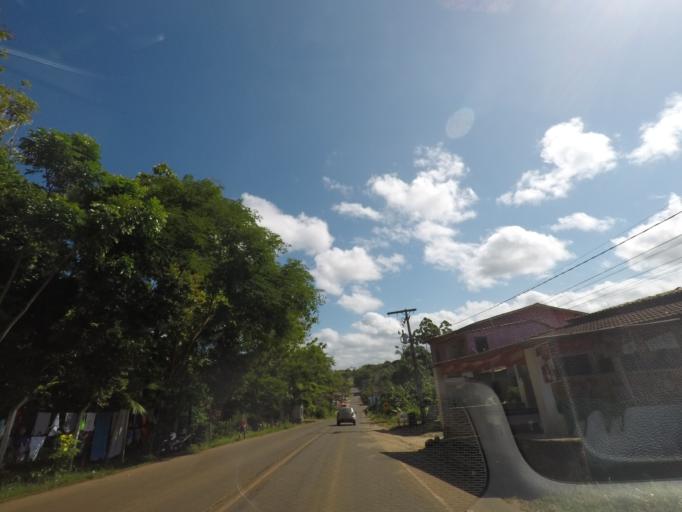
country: BR
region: Bahia
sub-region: Camamu
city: Camamu
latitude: -13.8909
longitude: -39.1384
